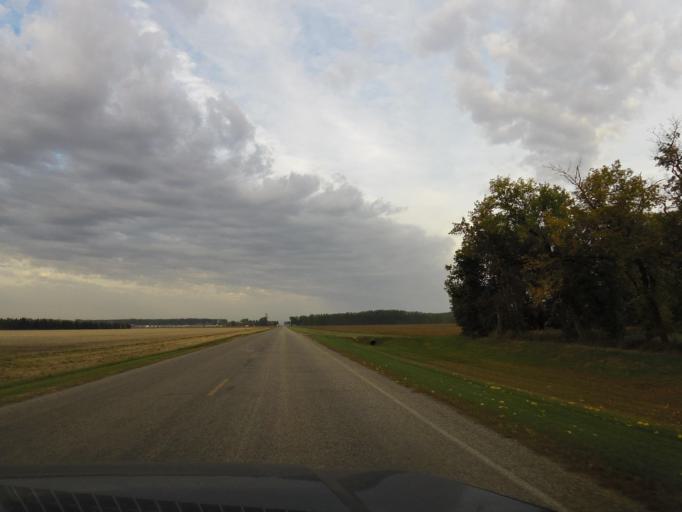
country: US
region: North Dakota
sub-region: Pembina County
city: Cavalier
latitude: 48.6881
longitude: -97.6464
